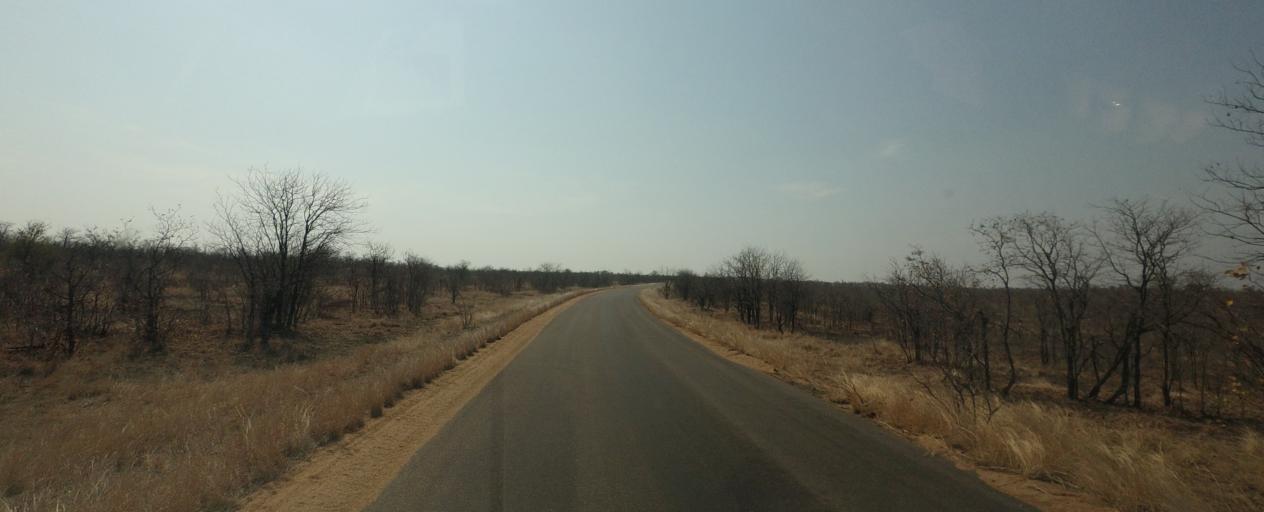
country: ZA
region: Limpopo
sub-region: Mopani District Municipality
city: Phalaborwa
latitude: -23.9775
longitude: 31.6378
